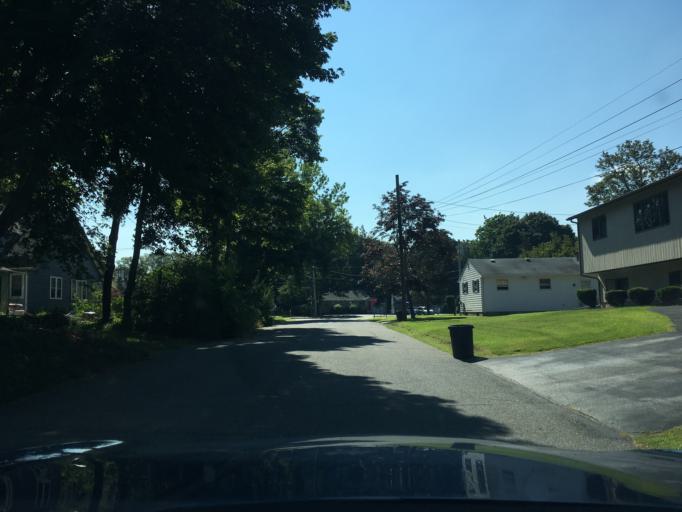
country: US
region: Rhode Island
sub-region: Kent County
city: East Greenwich
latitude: 41.6443
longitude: -71.4659
